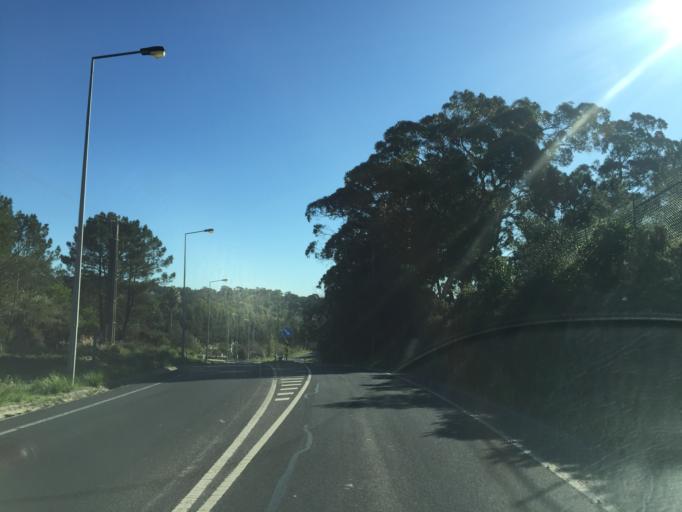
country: PT
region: Lisbon
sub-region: Sintra
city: Belas
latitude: 38.8020
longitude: -9.2831
